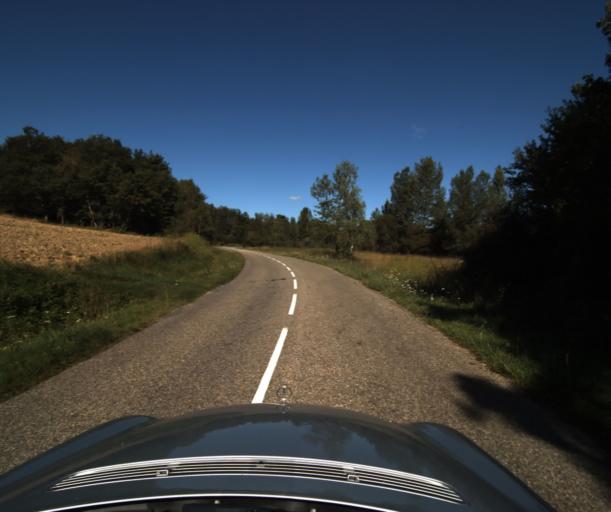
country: FR
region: Languedoc-Roussillon
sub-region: Departement de l'Aude
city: Chalabre
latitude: 42.9674
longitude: 1.9524
